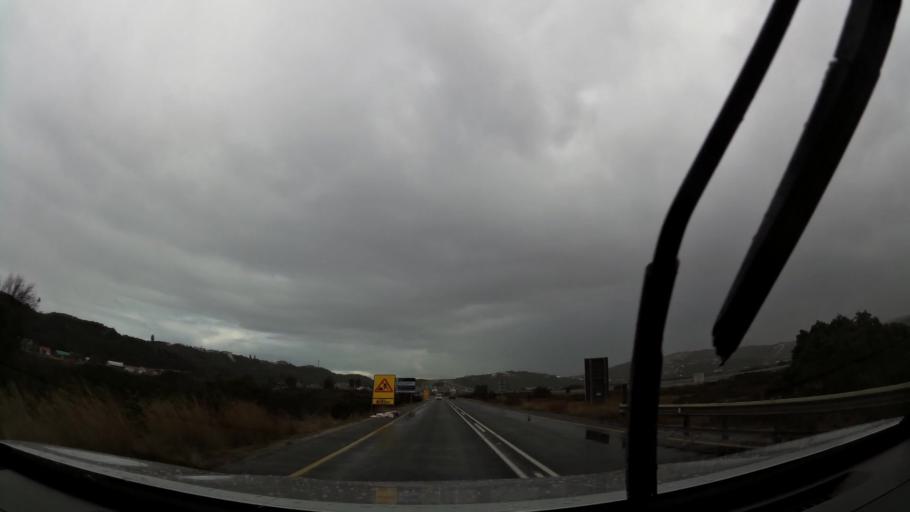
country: ZA
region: Western Cape
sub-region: Eden District Municipality
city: Mossel Bay
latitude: -34.0517
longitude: 22.2299
